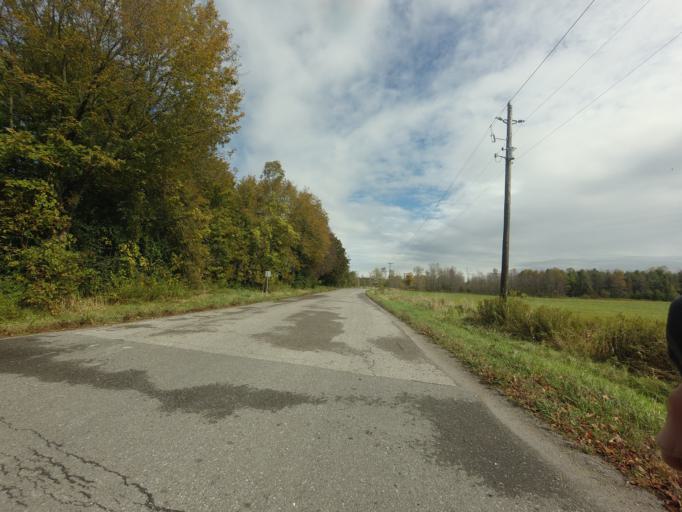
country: CA
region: Ontario
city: Cobourg
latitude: 43.9350
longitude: -78.3765
